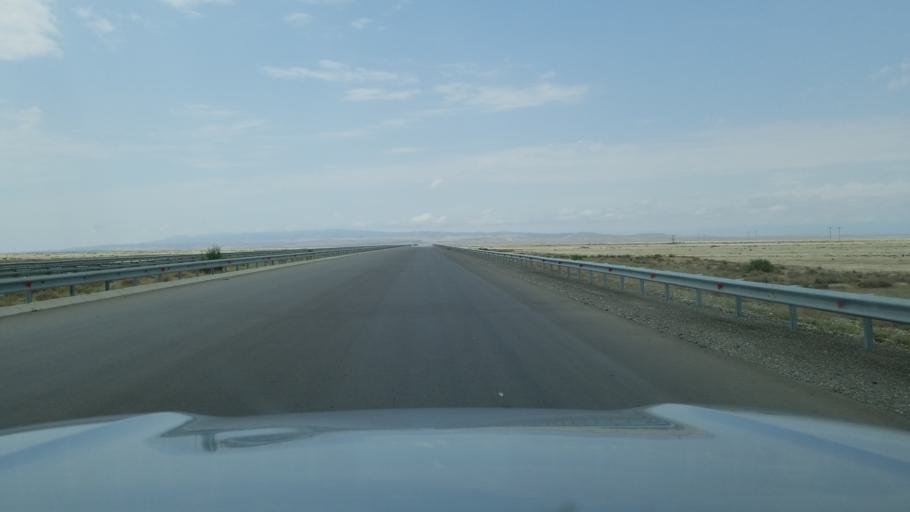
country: TM
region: Balkan
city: Gazanjyk
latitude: 39.2767
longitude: 55.2608
